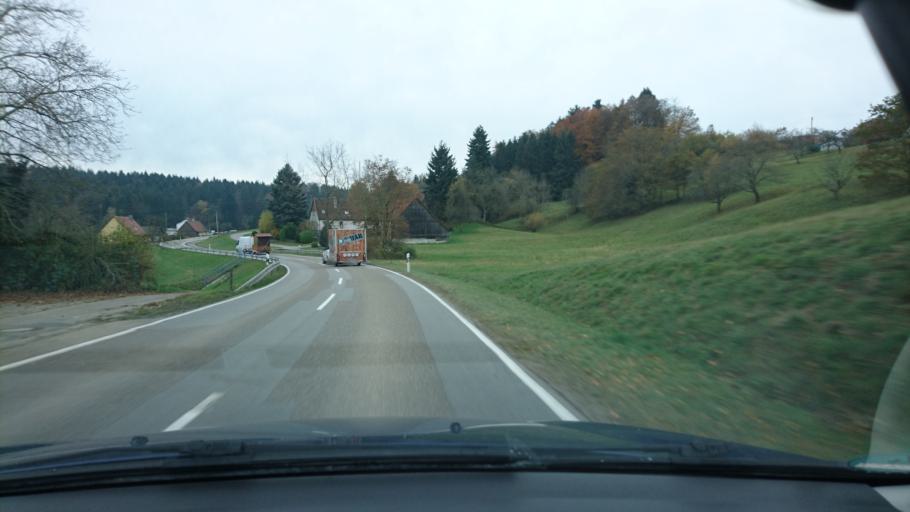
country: DE
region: Baden-Wuerttemberg
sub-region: Regierungsbezirk Stuttgart
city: Gschwend
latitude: 48.9347
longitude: 9.7235
